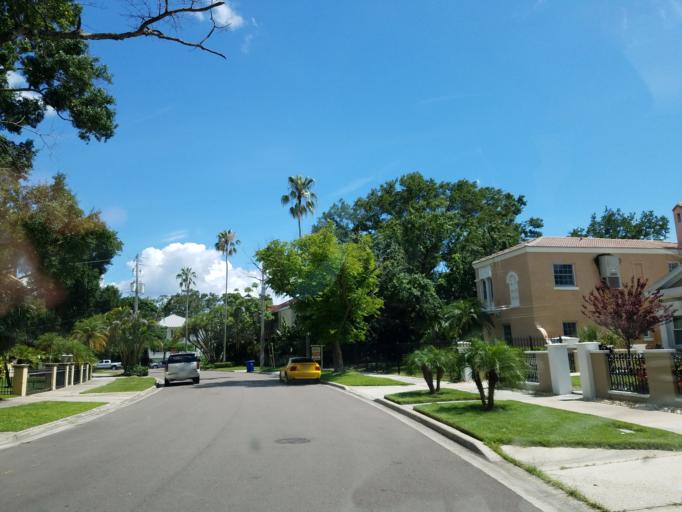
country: US
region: Florida
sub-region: Hillsborough County
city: Tampa
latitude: 27.9334
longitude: -82.4593
